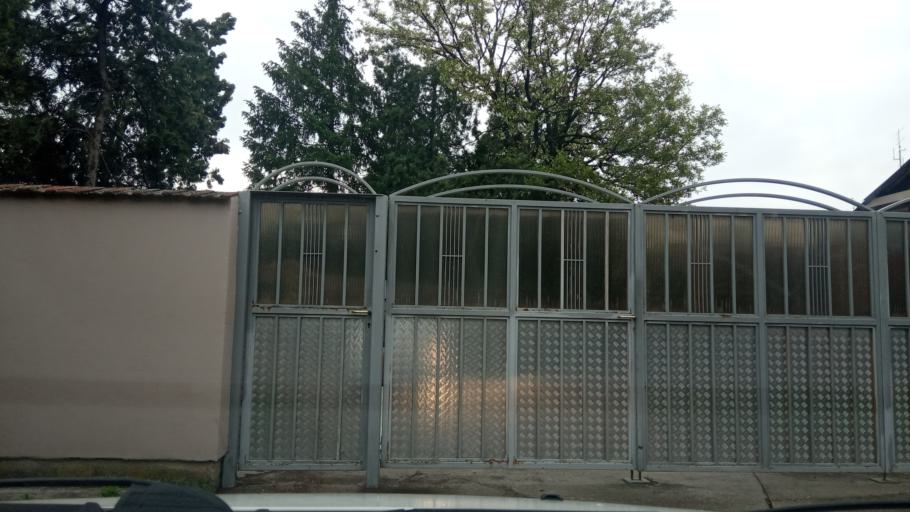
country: RS
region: Autonomna Pokrajina Vojvodina
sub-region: Sremski Okrug
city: Stara Pazova
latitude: 44.9851
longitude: 20.1554
